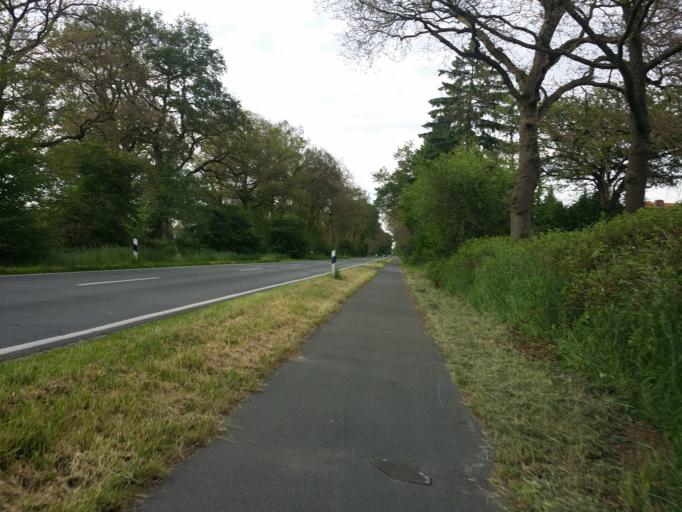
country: DE
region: Lower Saxony
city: Wittmund
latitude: 53.5342
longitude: 7.7819
